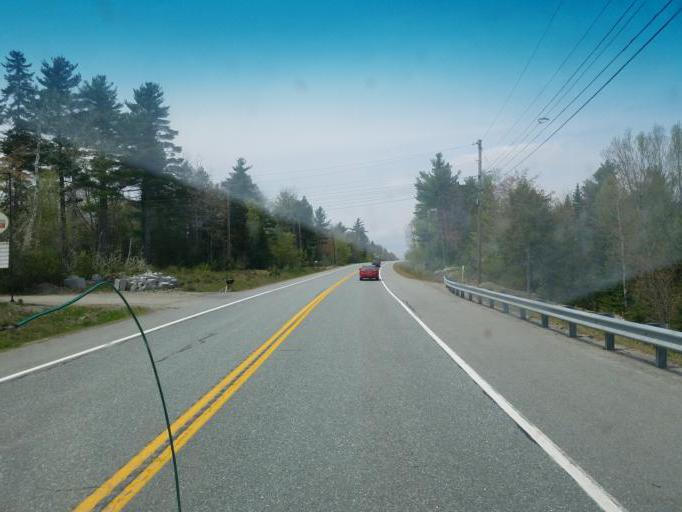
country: US
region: Maine
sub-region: Hancock County
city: Ellsworth
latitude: 44.5841
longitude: -68.4909
